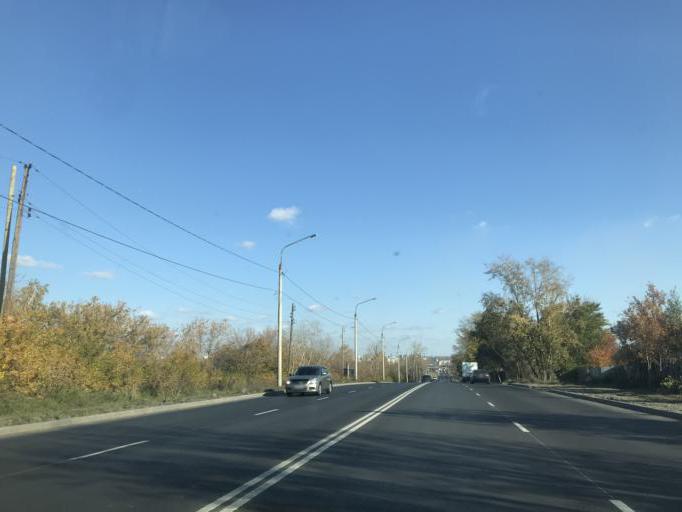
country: RU
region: Chelyabinsk
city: Roshchino
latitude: 55.2404
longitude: 61.3282
